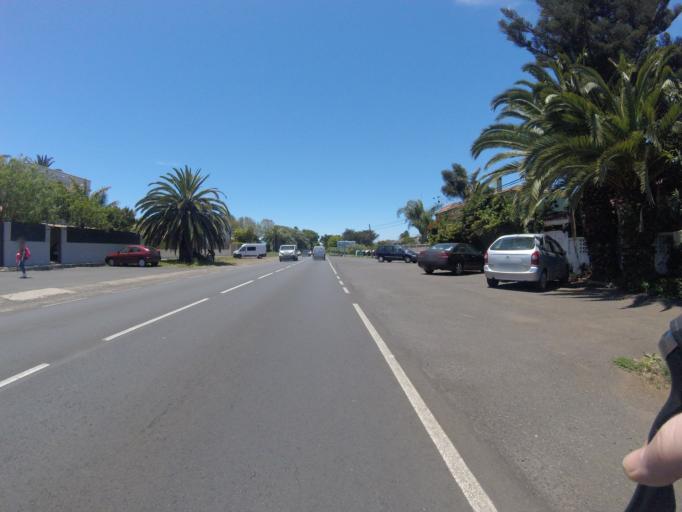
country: ES
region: Canary Islands
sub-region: Provincia de Santa Cruz de Tenerife
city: Tegueste
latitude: 28.5009
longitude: -16.3131
